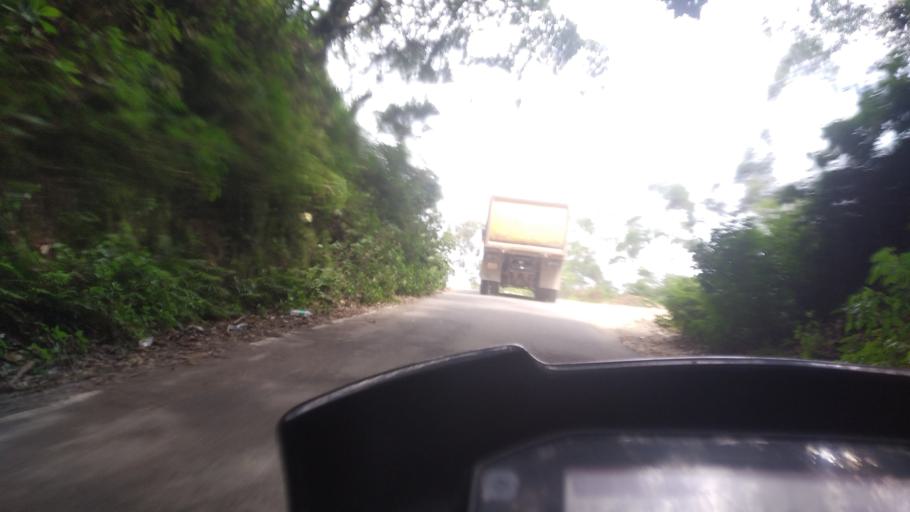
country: IN
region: Kerala
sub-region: Idukki
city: Munnar
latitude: 10.0367
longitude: 77.1223
